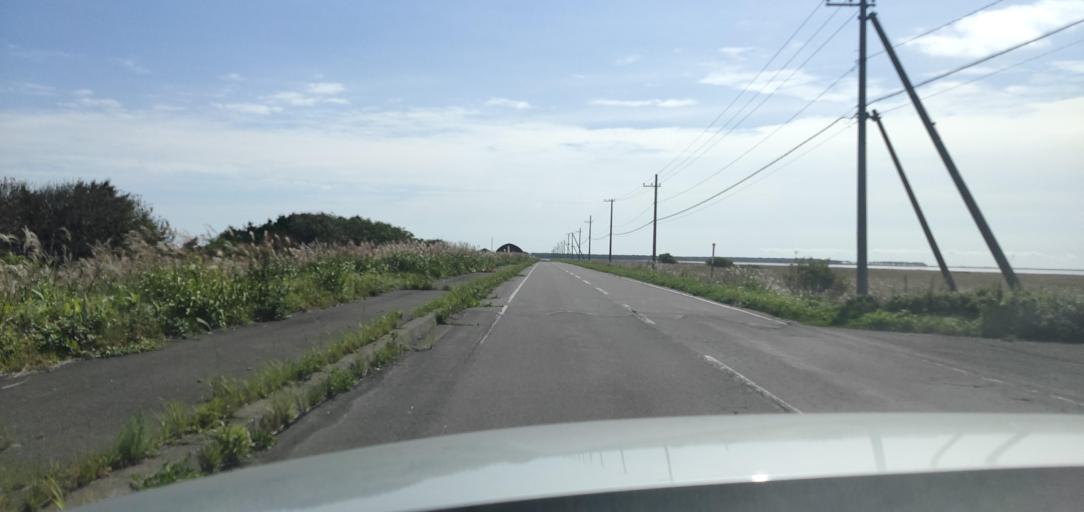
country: JP
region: Hokkaido
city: Shibetsu
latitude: 43.6190
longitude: 145.2309
